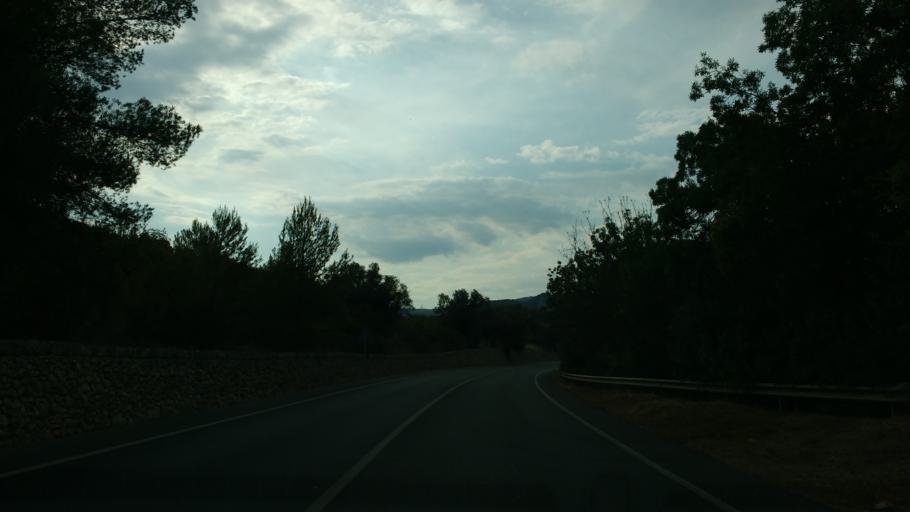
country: ES
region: Balearic Islands
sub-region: Illes Balears
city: Consell
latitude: 39.6862
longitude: 2.8092
